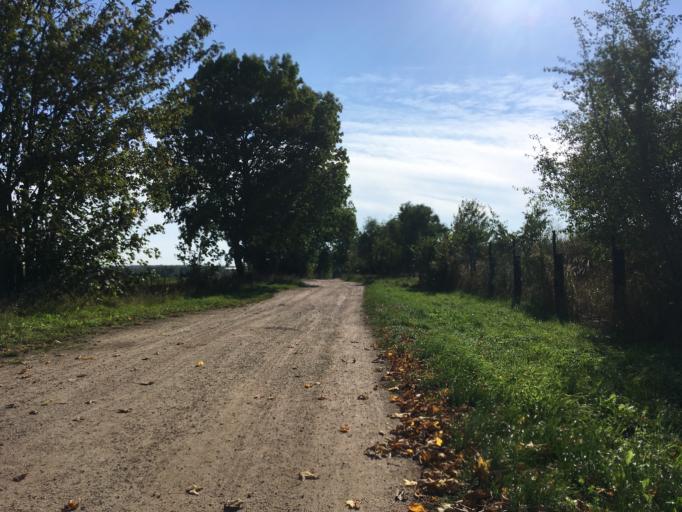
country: DE
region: Brandenburg
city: Altlandsberg
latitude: 52.5509
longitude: 13.7260
